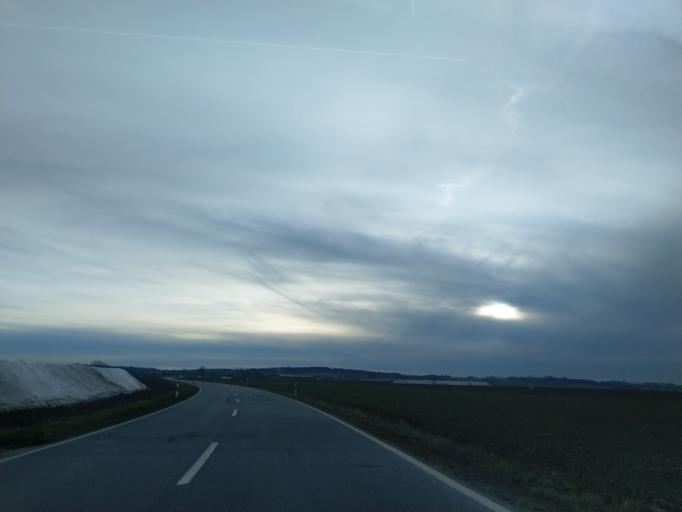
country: DE
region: Bavaria
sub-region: Lower Bavaria
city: Wallerfing
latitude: 48.7055
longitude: 12.8835
